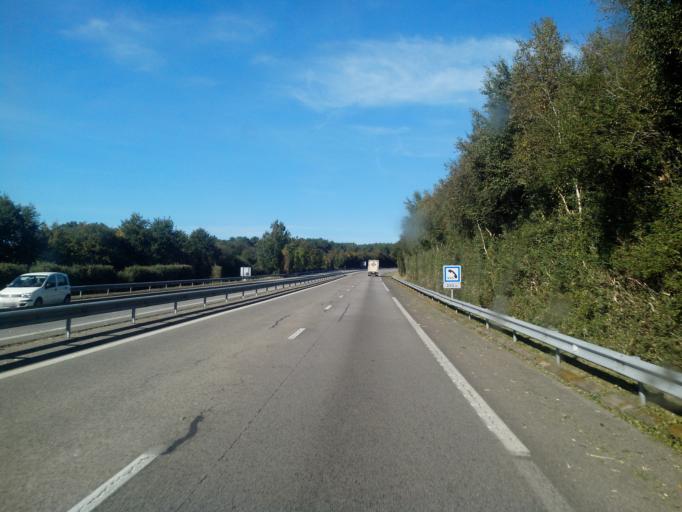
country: FR
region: Brittany
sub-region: Departement du Morbihan
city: Malestroit
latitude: 47.8071
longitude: -2.4435
